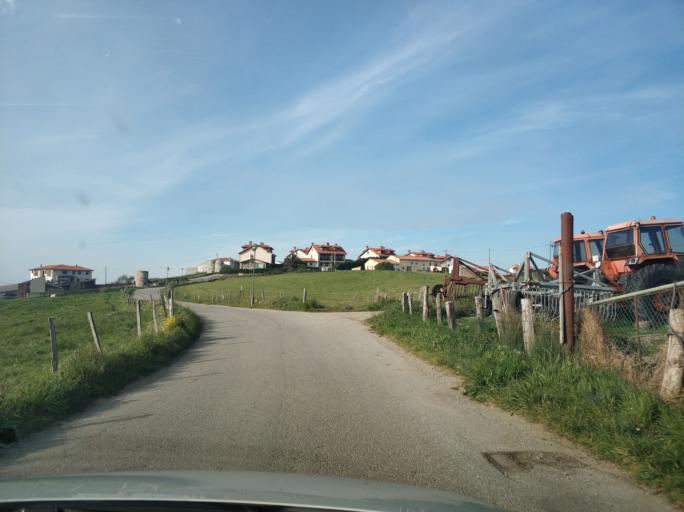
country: ES
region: Cantabria
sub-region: Provincia de Cantabria
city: San Vicente de la Barquera
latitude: 43.3969
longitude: -4.3507
